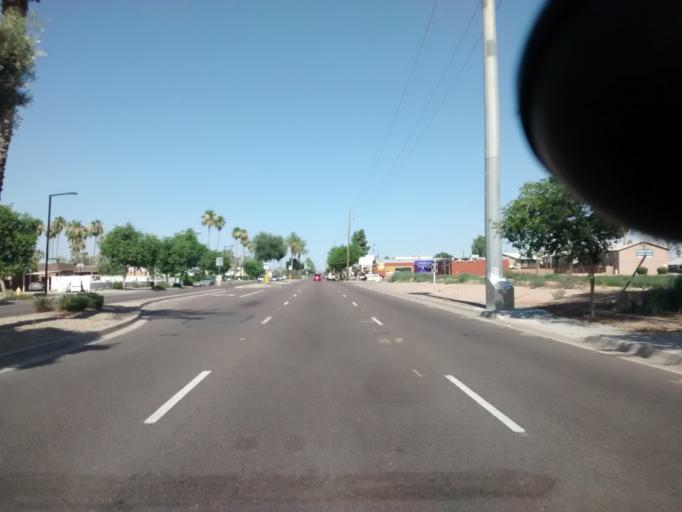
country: US
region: Arizona
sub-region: Maricopa County
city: Peoria
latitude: 33.5378
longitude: -112.2326
